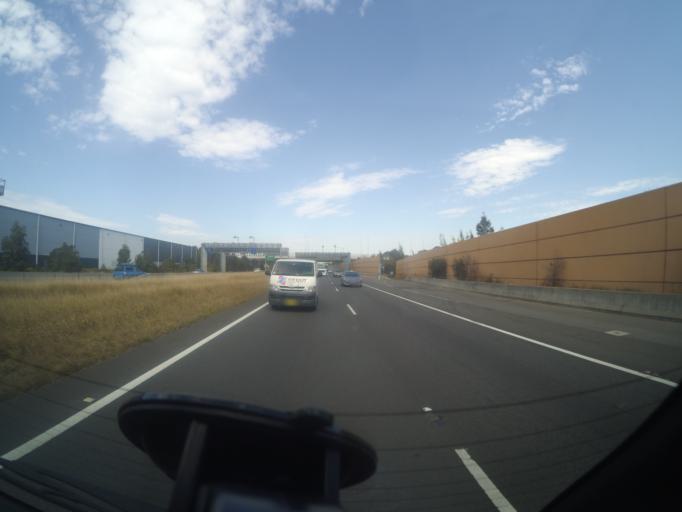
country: AU
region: New South Wales
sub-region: Liverpool
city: Miller
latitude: -33.9421
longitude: 150.8786
